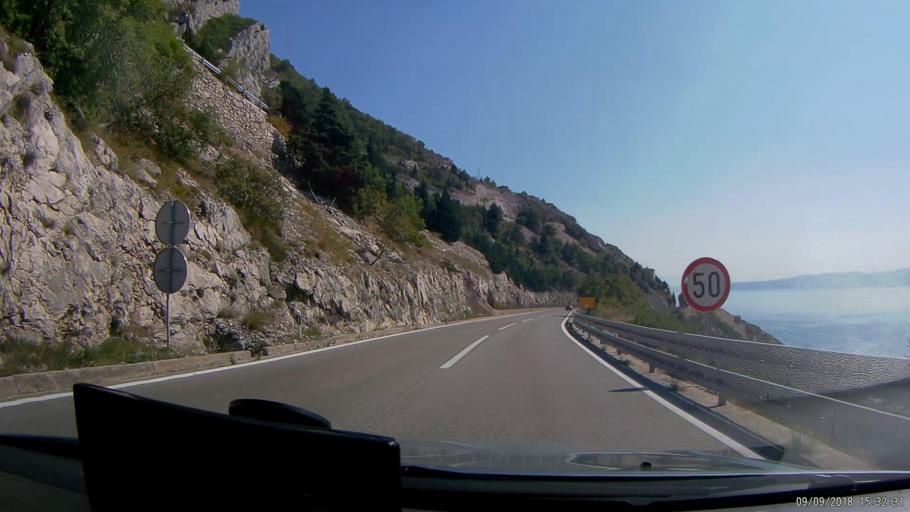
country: HR
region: Splitsko-Dalmatinska
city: Donja Brela
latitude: 43.4009
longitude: 16.8932
